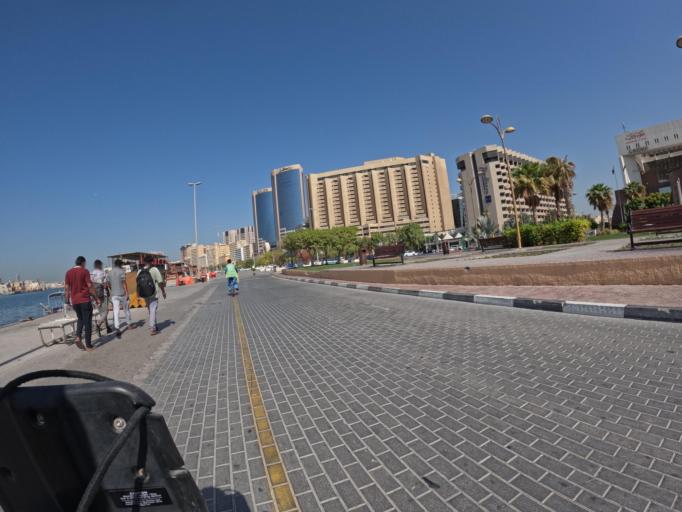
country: AE
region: Ash Shariqah
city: Sharjah
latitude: 25.2637
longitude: 55.3106
